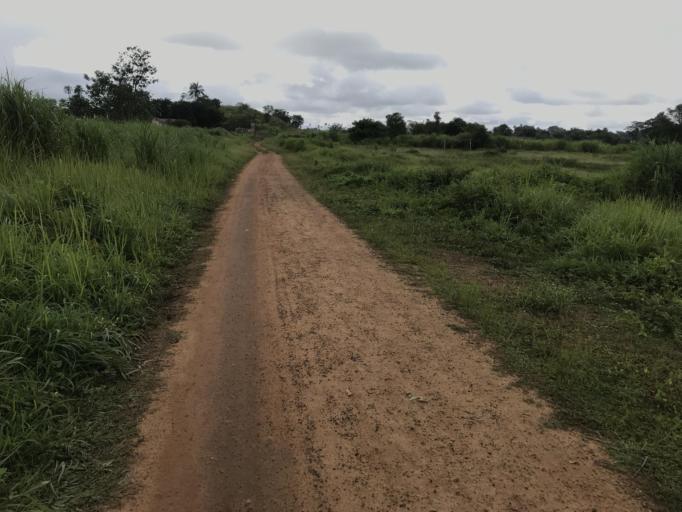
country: GN
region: Nzerekore
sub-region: Prefecture de Guekedou
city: Gueckedou
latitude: 8.4724
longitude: -10.2812
